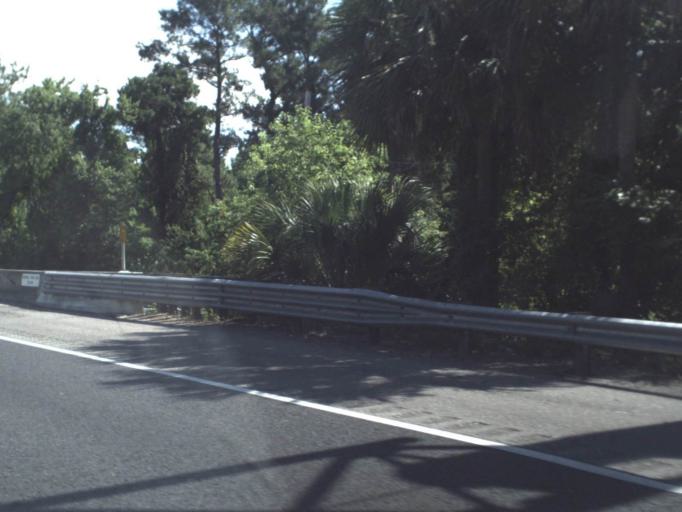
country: US
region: Florida
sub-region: Duval County
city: Jacksonville
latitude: 30.3049
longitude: -81.7701
